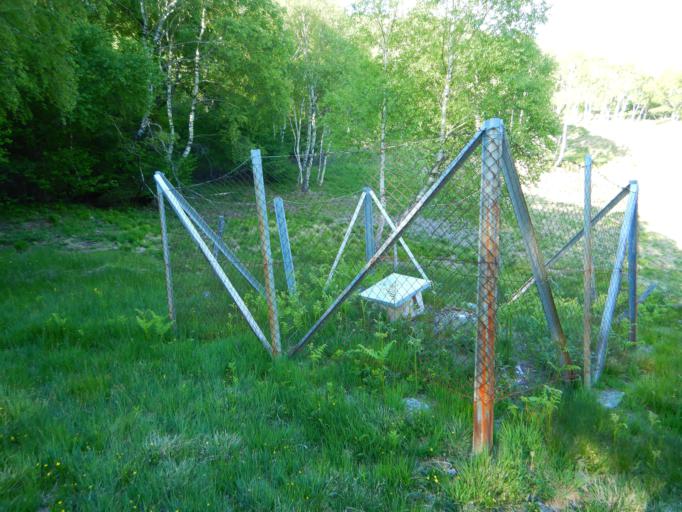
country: CH
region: Ticino
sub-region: Bellinzona District
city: Cadenazzo
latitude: 46.1309
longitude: 8.9556
